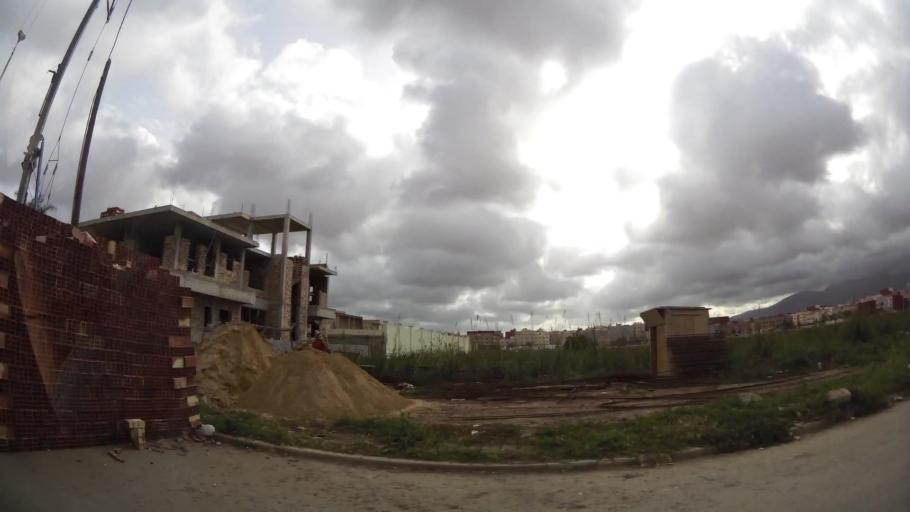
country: MA
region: Oriental
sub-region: Nador
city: Nador
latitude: 35.1635
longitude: -2.9168
